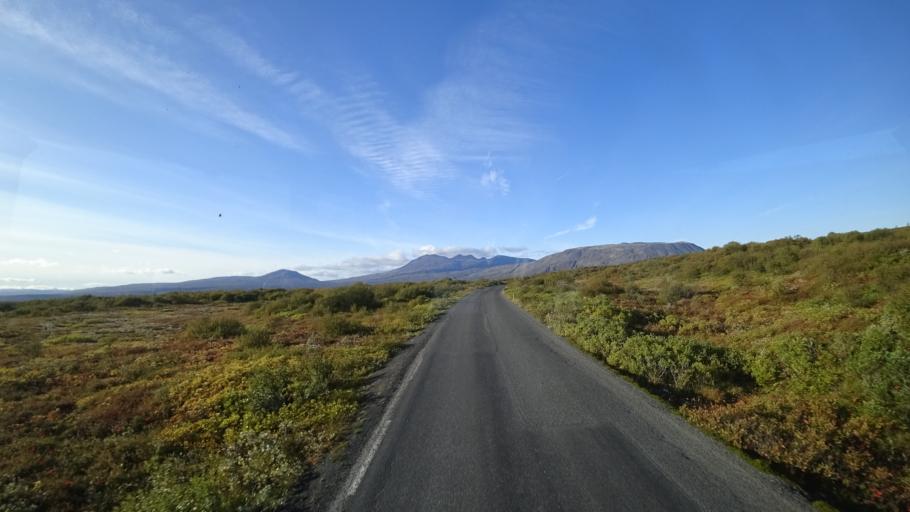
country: IS
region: South
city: Hveragerdi
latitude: 64.2536
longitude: -21.0263
